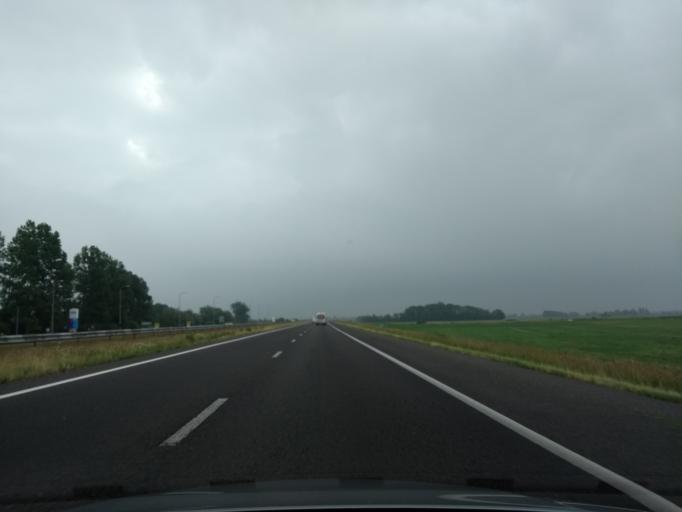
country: NL
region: Friesland
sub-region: Sudwest Fryslan
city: Oppenhuizen
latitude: 52.9846
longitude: 5.7330
